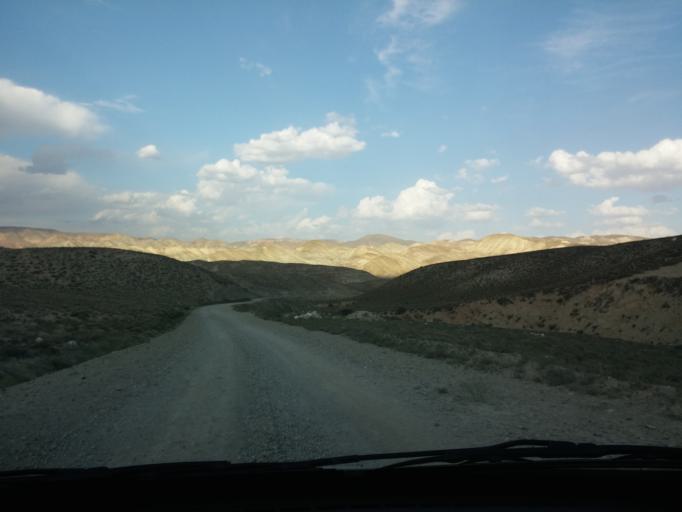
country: IR
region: Tehran
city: Damavand
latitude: 35.5326
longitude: 52.2281
